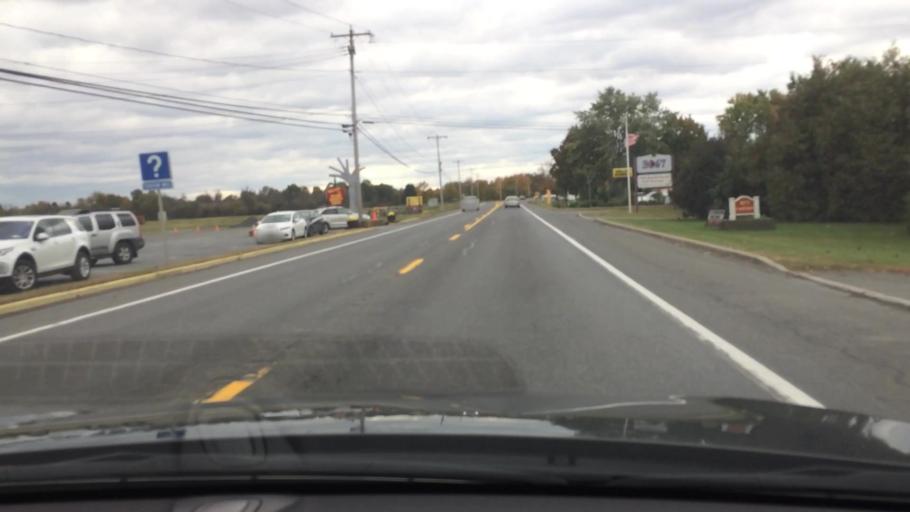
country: US
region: New York
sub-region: Columbia County
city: Valatie
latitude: 42.4356
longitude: -73.6870
